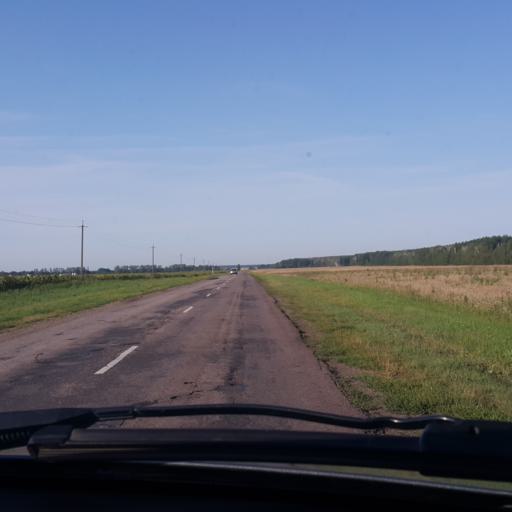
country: RU
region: Tambov
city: Novaya Lyada
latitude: 52.7668
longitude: 41.7396
